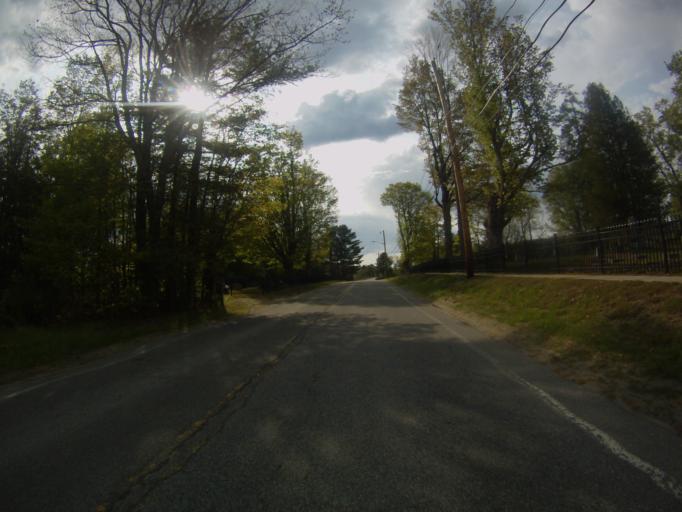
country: US
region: New York
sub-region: Warren County
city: Warrensburg
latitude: 43.8331
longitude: -73.7686
